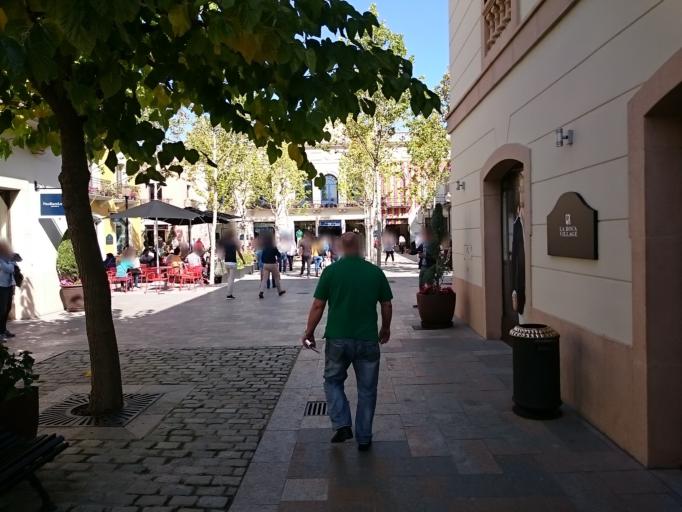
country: ES
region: Catalonia
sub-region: Provincia de Barcelona
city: Cardedeu
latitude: 41.6119
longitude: 2.3450
